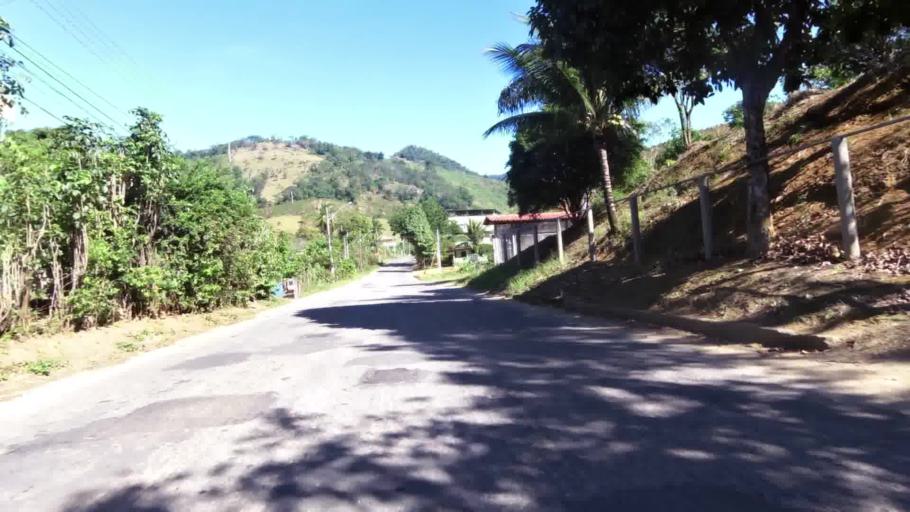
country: BR
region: Espirito Santo
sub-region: Iconha
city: Iconha
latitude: -20.7793
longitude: -40.8253
